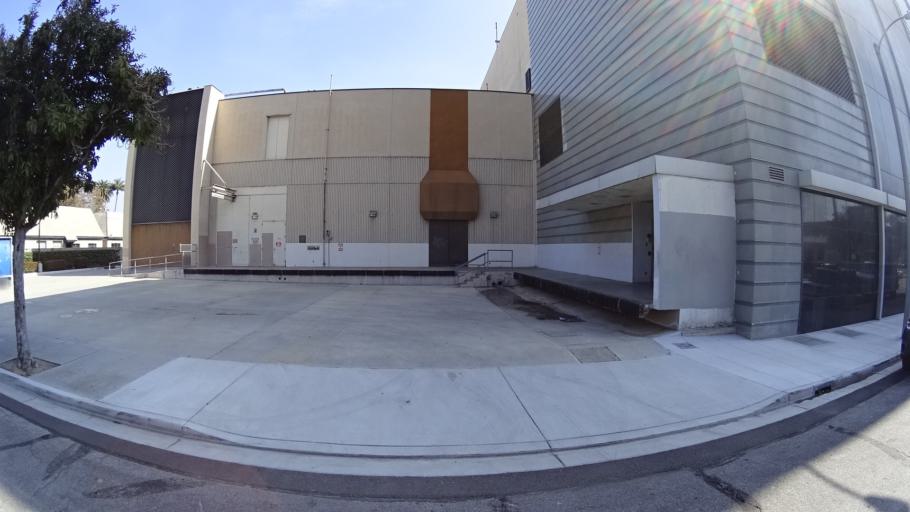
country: US
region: California
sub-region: Orange County
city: Anaheim
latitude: 33.8365
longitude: -117.9176
